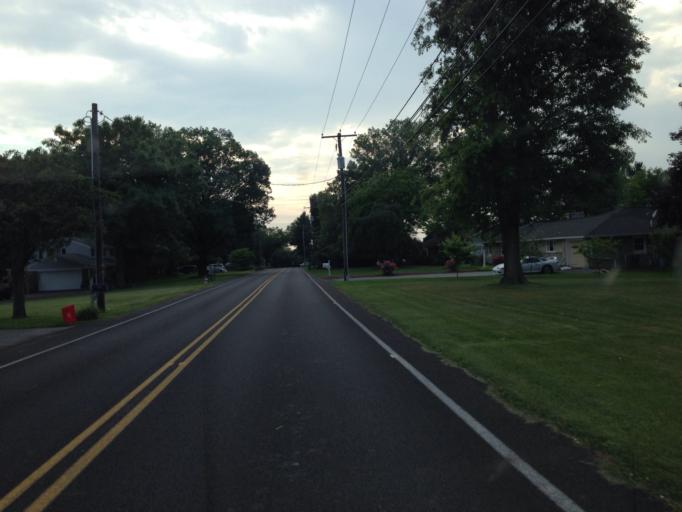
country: US
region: Pennsylvania
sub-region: Lancaster County
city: Lititz
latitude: 40.1432
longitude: -76.2904
